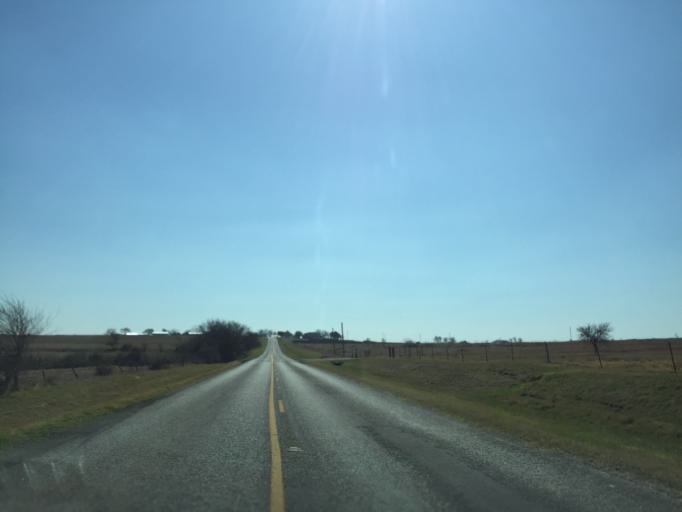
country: US
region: Texas
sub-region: Williamson County
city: Serenada
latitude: 30.7216
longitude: -97.5817
